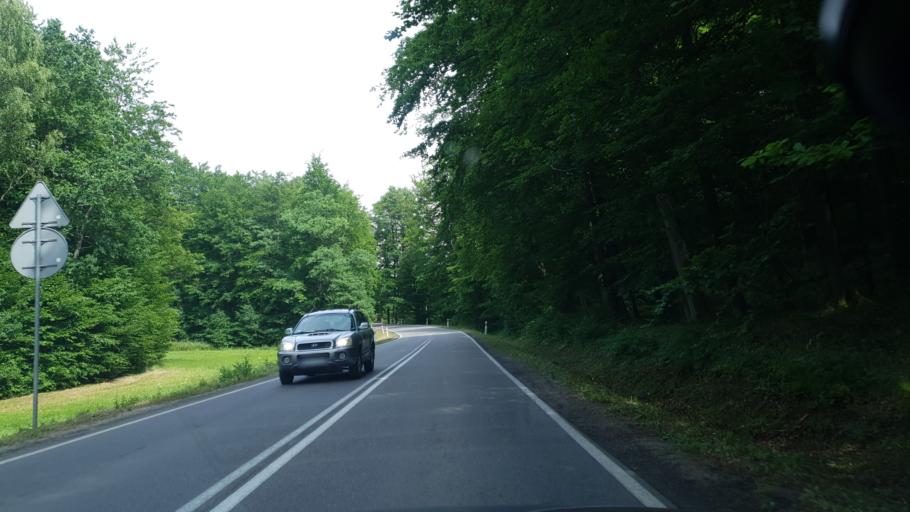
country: PL
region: Pomeranian Voivodeship
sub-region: Powiat kartuski
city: Kartuzy
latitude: 54.3169
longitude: 18.1693
